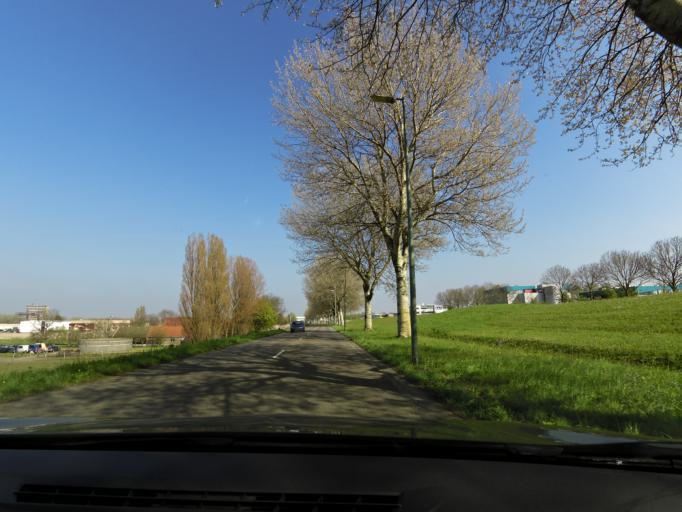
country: NL
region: South Holland
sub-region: Gemeente Vlaardingen
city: Vlaardingen
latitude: 51.9015
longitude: 4.3033
